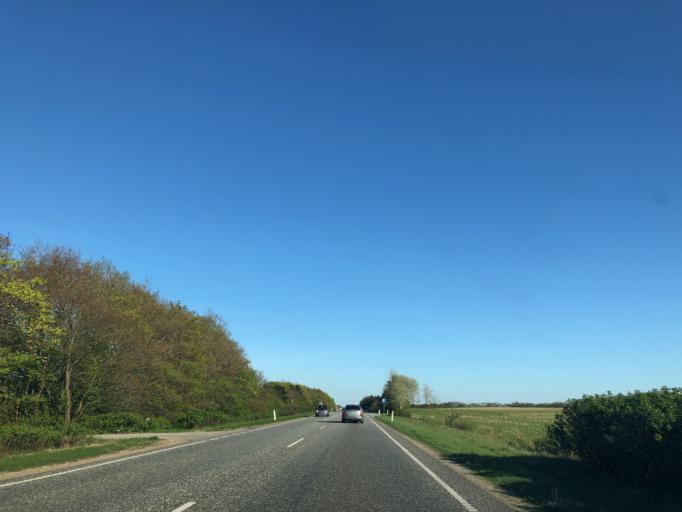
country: DK
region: Central Jutland
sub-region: Herning Kommune
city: Avlum
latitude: 56.3009
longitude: 8.7142
